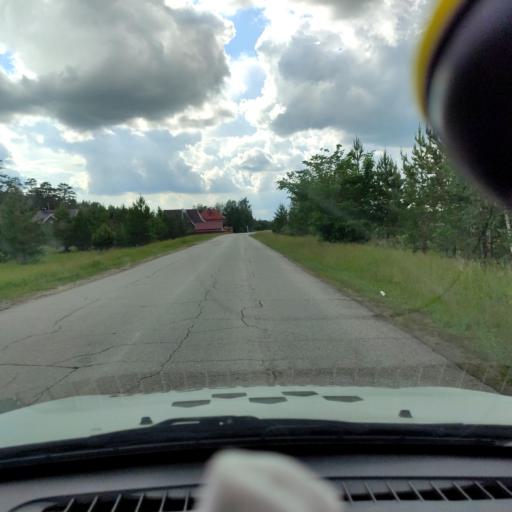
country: RU
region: Samara
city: Povolzhskiy
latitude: 53.6478
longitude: 49.7227
